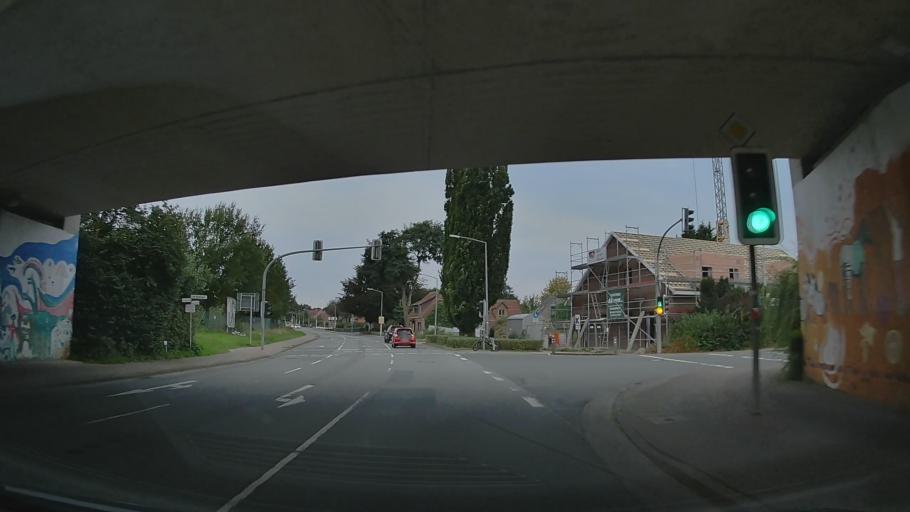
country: DE
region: Lower Saxony
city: Syke
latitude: 52.9110
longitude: 8.8102
